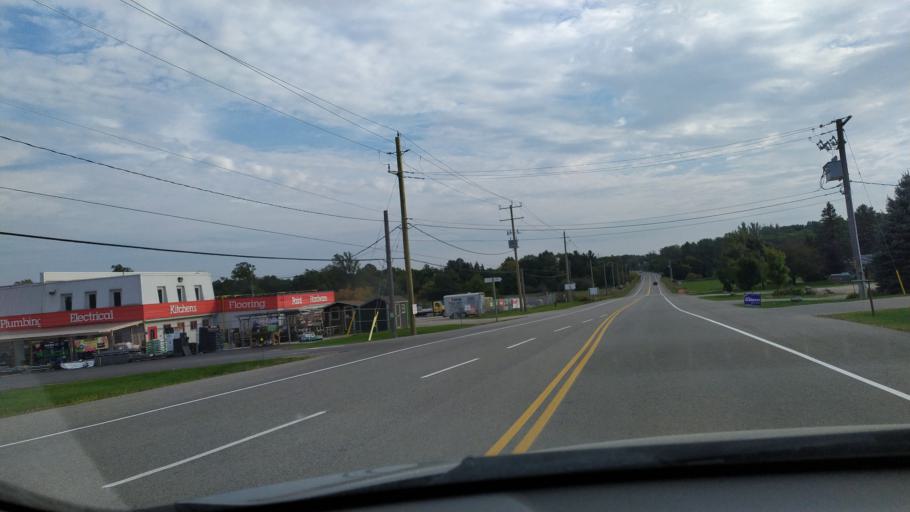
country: CA
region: Ontario
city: Stratford
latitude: 43.4698
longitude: -80.7654
